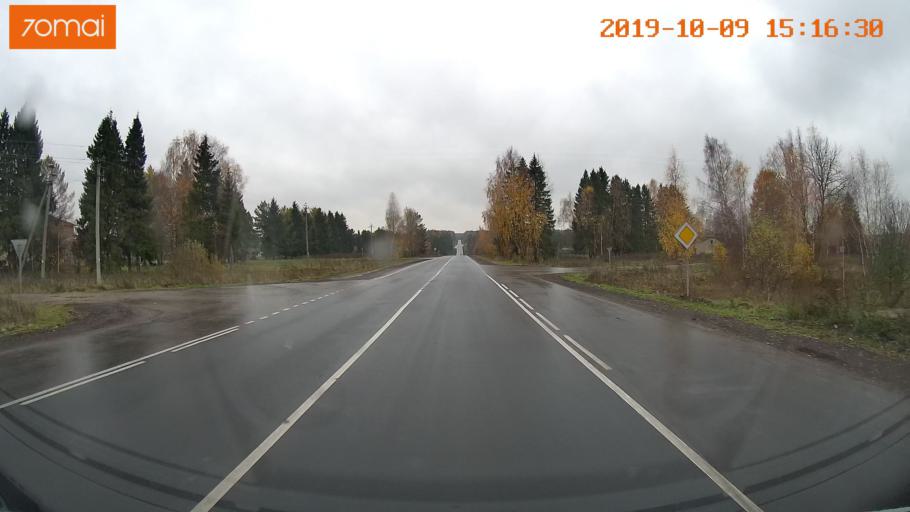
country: RU
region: Kostroma
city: Susanino
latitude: 58.1098
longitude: 41.5858
